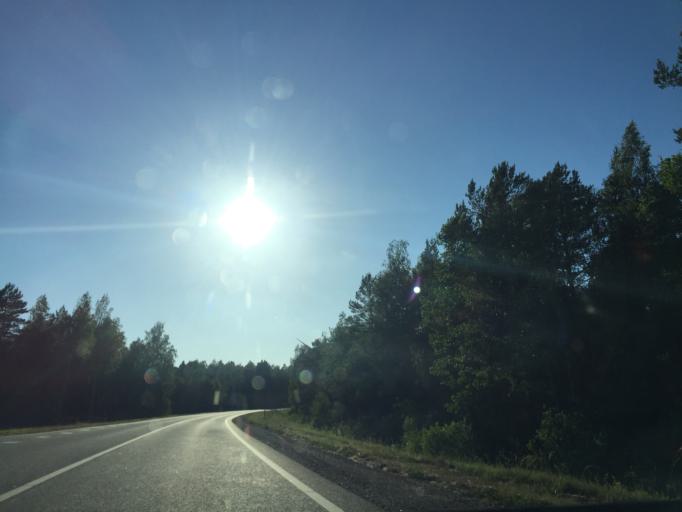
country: LV
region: Ventspils Rajons
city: Piltene
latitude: 57.3777
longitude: 21.7214
